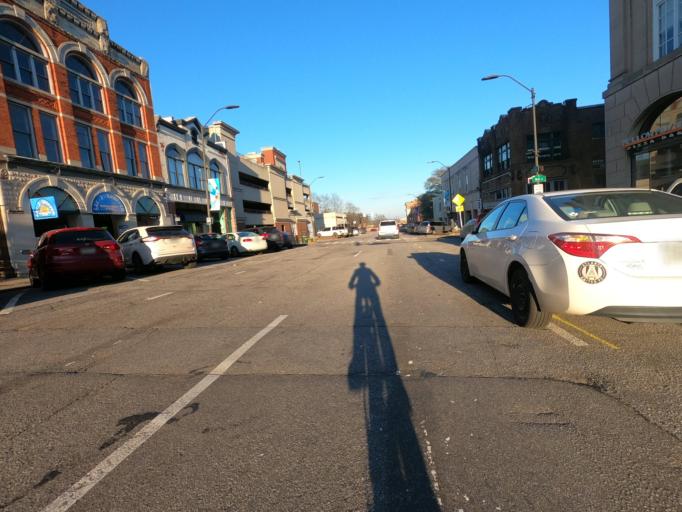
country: US
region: Georgia
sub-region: Clarke County
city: Athens
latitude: 33.9588
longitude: -83.3743
